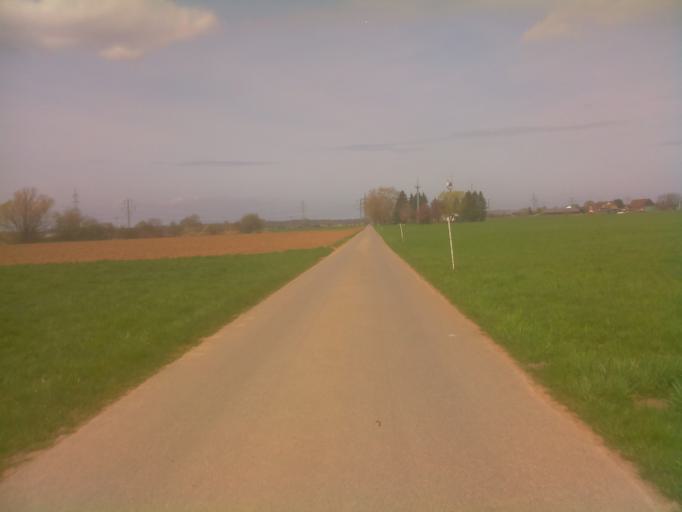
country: DE
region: Baden-Wuerttemberg
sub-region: Karlsruhe Region
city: Hemsbach
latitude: 49.5708
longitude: 8.6248
